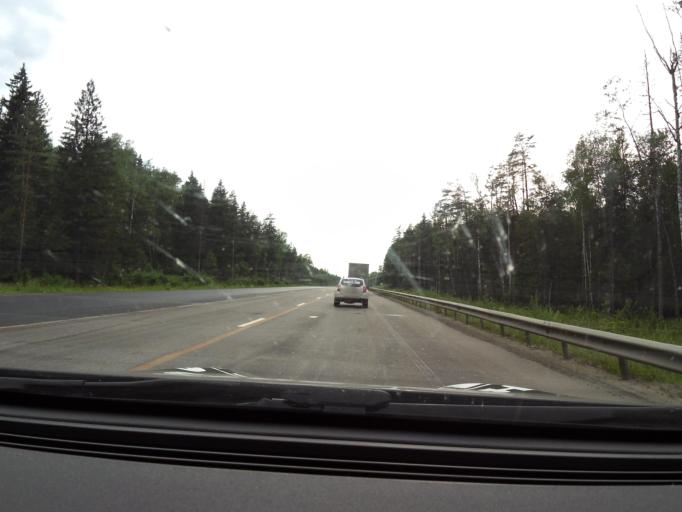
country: RU
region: Vladimir
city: Mstera
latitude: 56.2344
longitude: 41.8405
